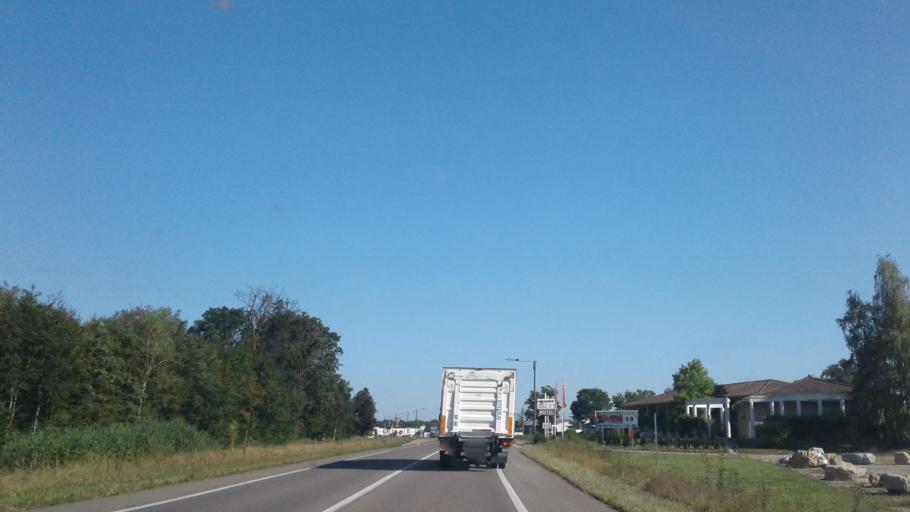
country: FR
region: Rhone-Alpes
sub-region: Departement de l'Ain
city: Montagnat
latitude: 46.1701
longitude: 5.2613
